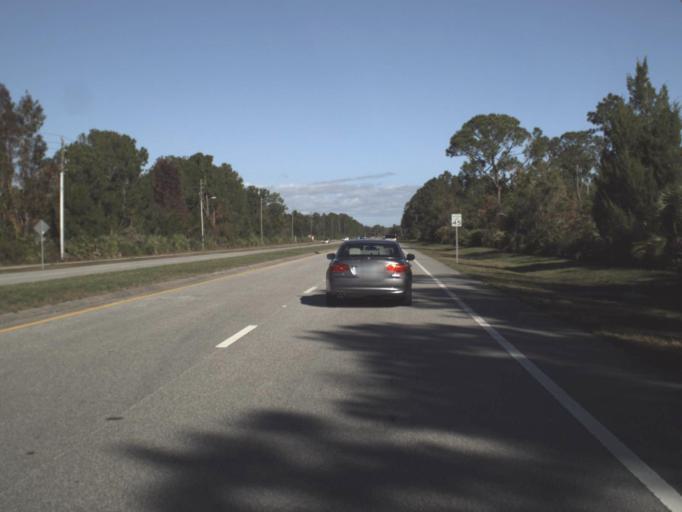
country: US
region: Florida
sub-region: Volusia County
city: Ormond Beach
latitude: 29.2503
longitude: -81.0937
